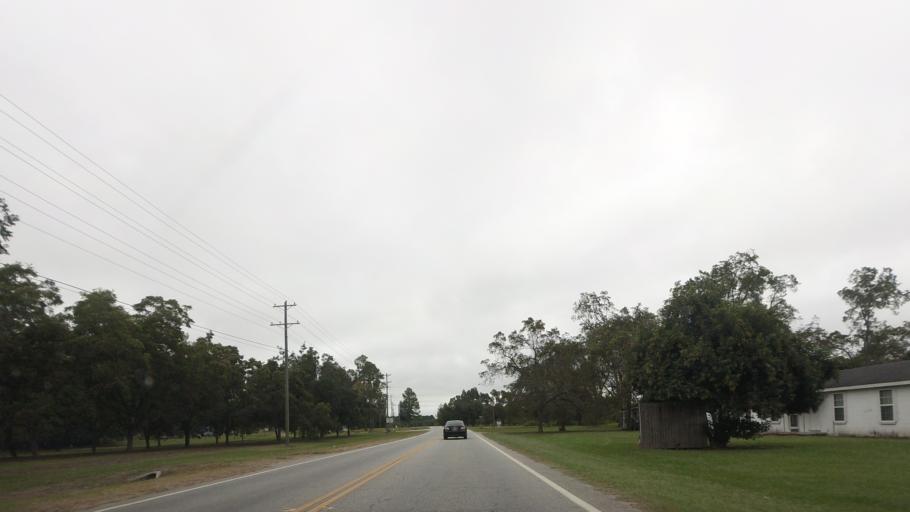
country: US
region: Georgia
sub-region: Berrien County
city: Ray City
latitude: 31.0031
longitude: -83.1990
